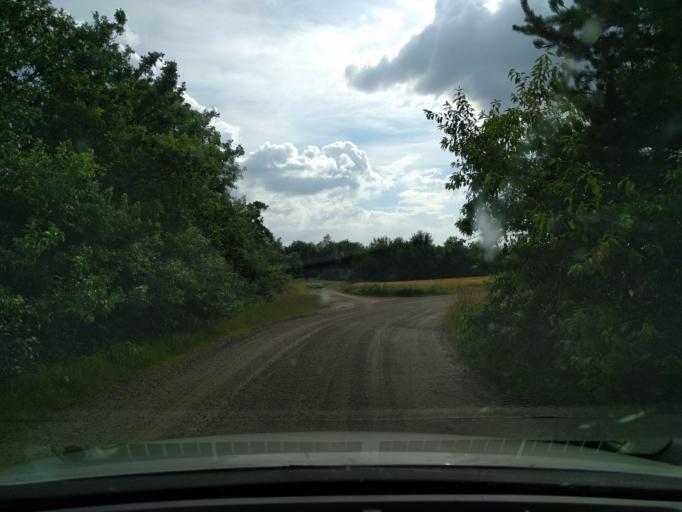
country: DK
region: Central Jutland
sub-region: Herning Kommune
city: Kibaek
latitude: 56.0661
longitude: 8.8945
